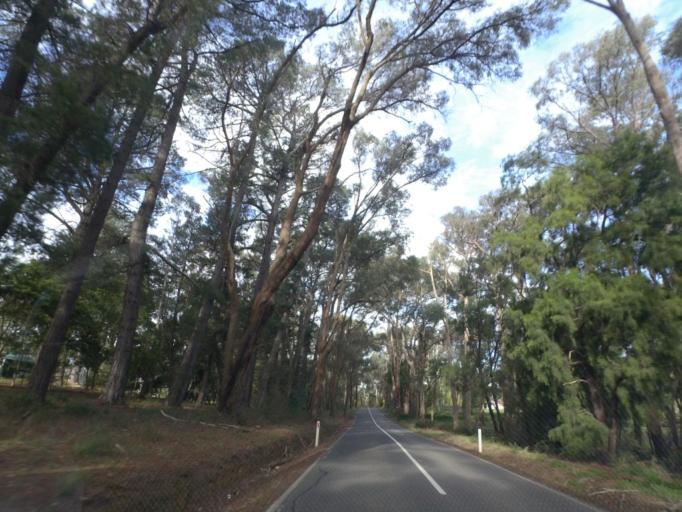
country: AU
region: Victoria
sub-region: Yarra Ranges
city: Mount Evelyn
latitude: -37.7666
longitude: 145.4013
